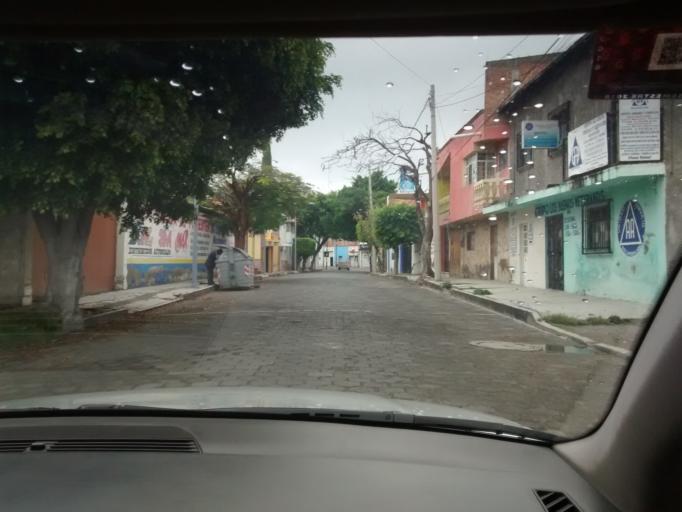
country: MX
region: Puebla
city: Tehuacan
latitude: 18.4603
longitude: -97.3993
